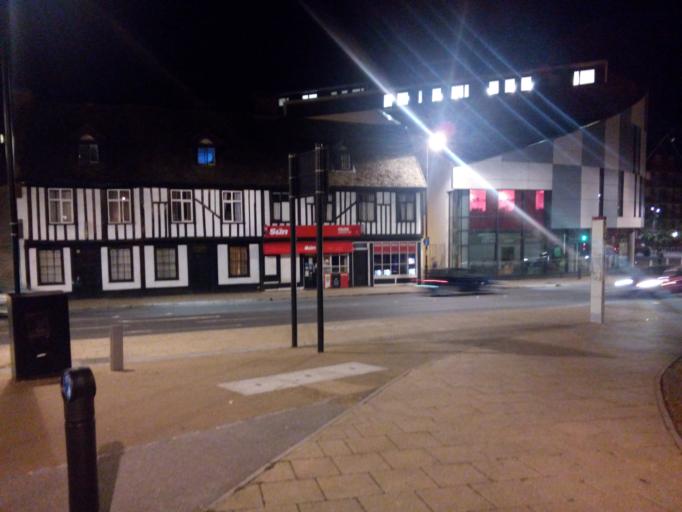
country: GB
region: England
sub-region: Suffolk
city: Ipswich
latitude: 52.0529
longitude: 1.1644
